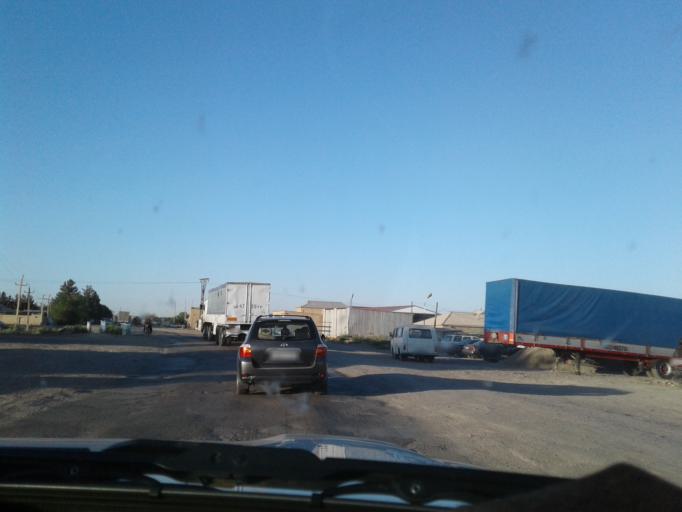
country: TM
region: Mary
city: Mary
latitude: 37.5703
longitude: 61.8515
